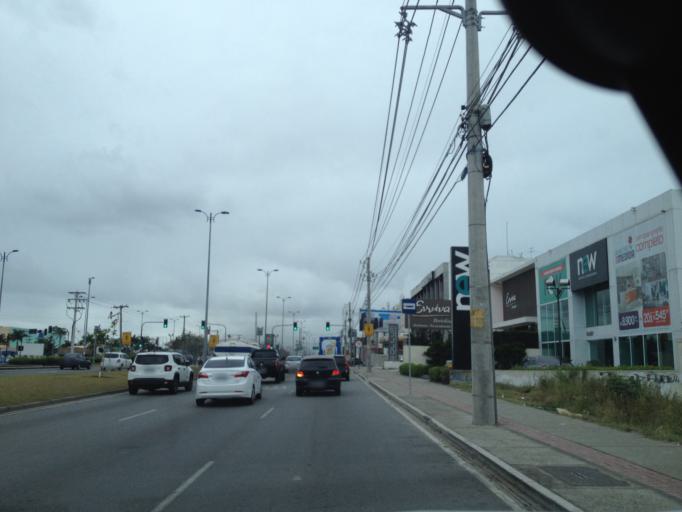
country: BR
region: Rio de Janeiro
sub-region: Nilopolis
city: Nilopolis
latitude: -23.0160
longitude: -43.4718
